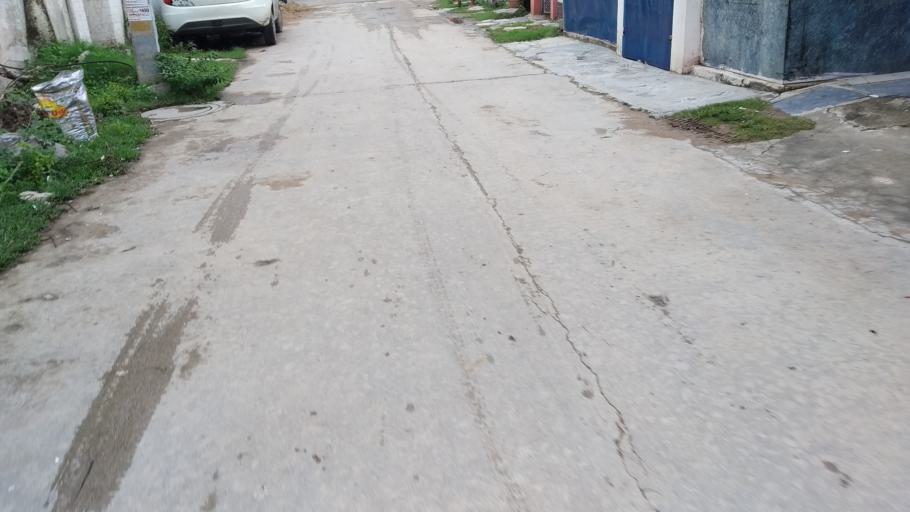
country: IN
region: Telangana
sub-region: Rangareddi
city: Kukatpalli
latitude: 17.4634
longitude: 78.4271
